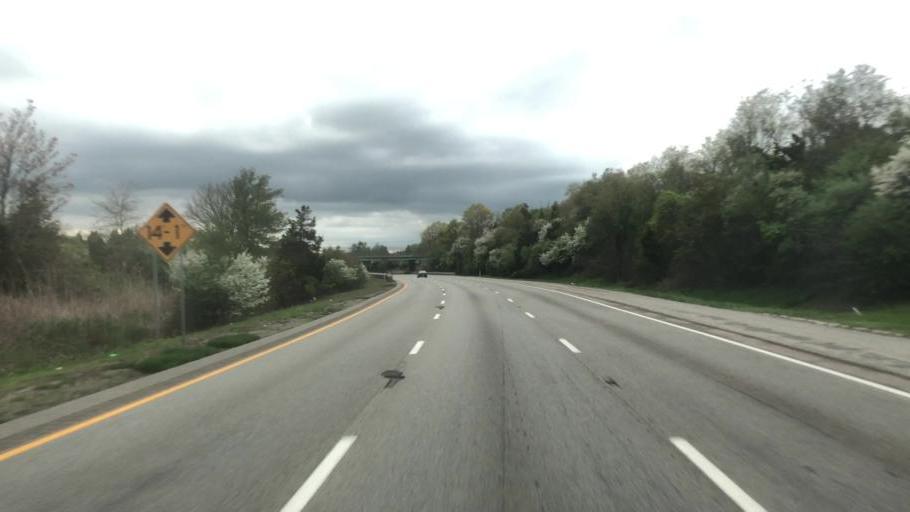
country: US
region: Massachusetts
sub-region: Bristol County
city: Swansea
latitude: 41.7269
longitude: -71.1860
